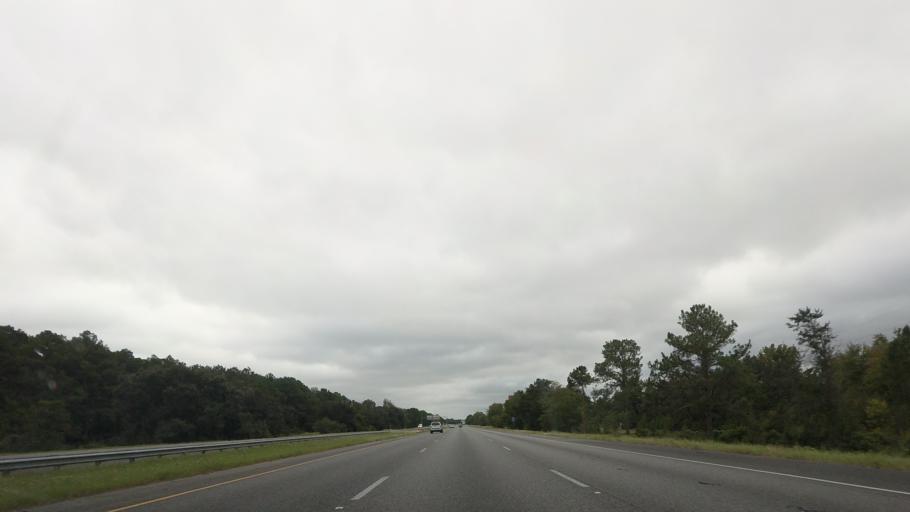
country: US
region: Georgia
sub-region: Echols County
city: Statenville
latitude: 30.6394
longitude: -83.1855
